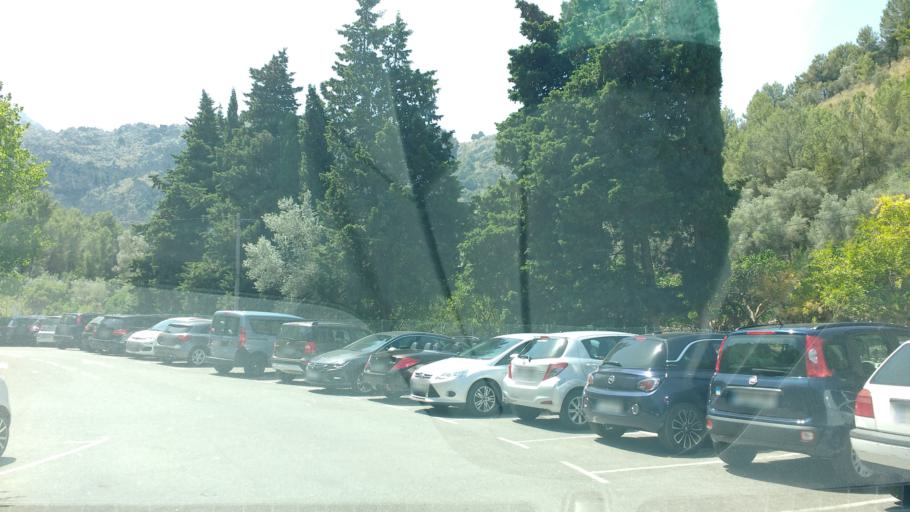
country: ES
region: Balearic Islands
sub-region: Illes Balears
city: Escorca
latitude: 39.8471
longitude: 2.7982
